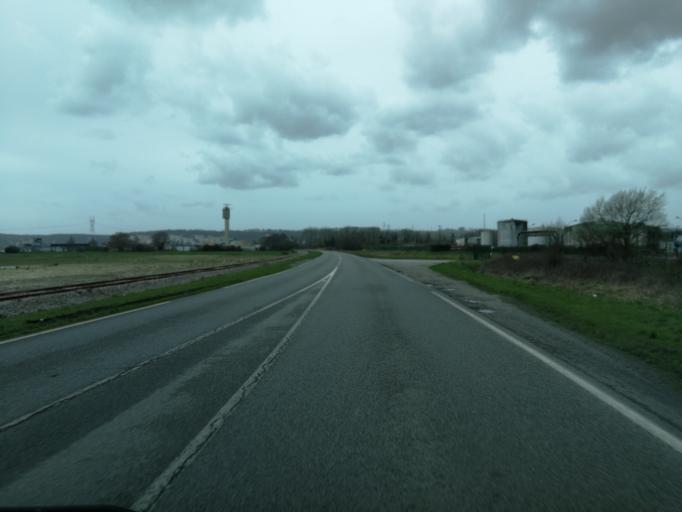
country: FR
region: Haute-Normandie
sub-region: Departement de l'Eure
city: Quillebeuf-sur-Seine
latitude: 49.4874
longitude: 0.5152
